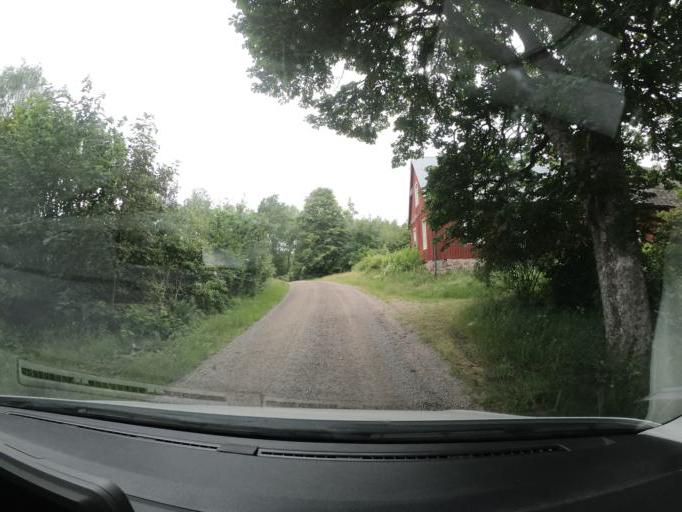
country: SE
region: Skane
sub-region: Hassleholms Kommun
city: Sosdala
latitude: 56.1014
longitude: 13.5479
